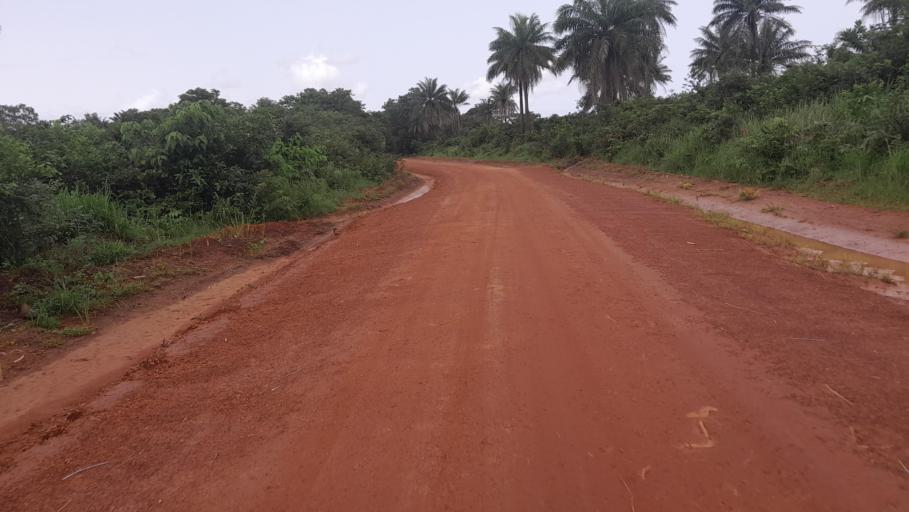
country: GN
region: Boke
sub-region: Boffa
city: Boffa
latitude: 10.0557
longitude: -13.8707
